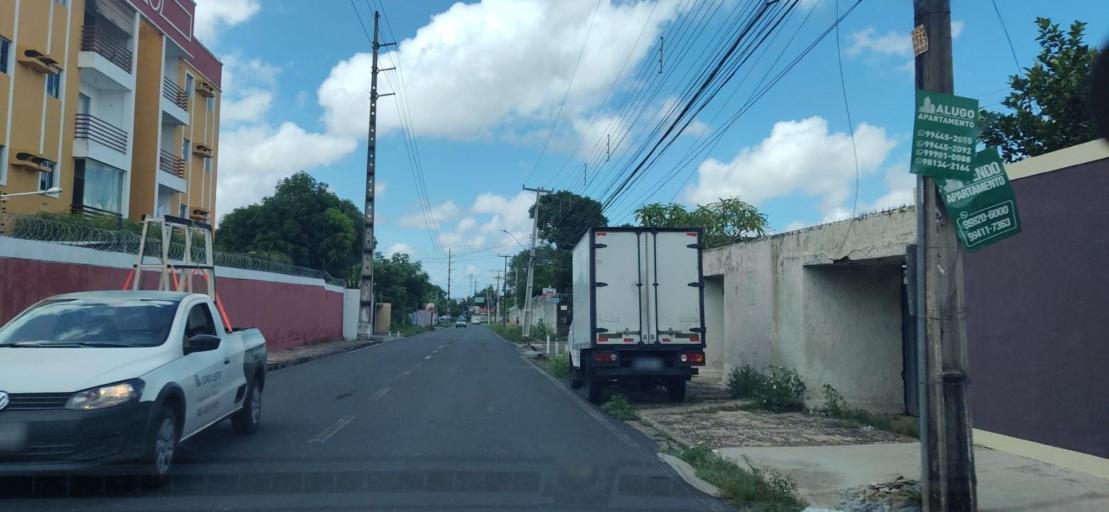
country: BR
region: Piaui
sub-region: Teresina
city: Teresina
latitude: -5.0682
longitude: -42.7603
